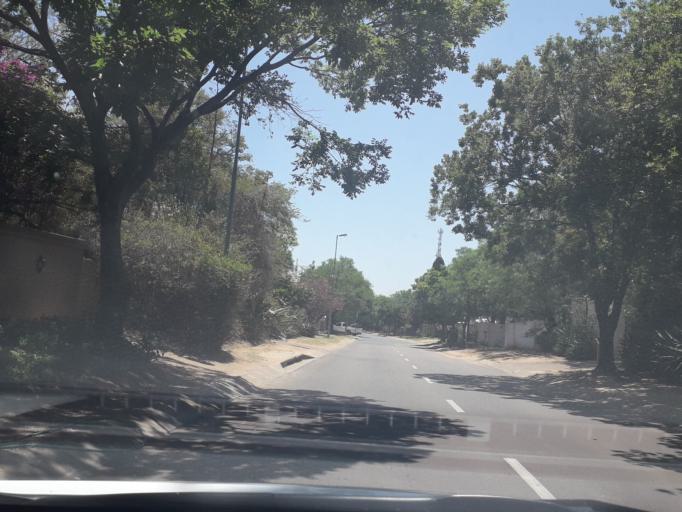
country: ZA
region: Gauteng
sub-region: City of Johannesburg Metropolitan Municipality
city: Diepsloot
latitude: -26.0252
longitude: 28.0082
